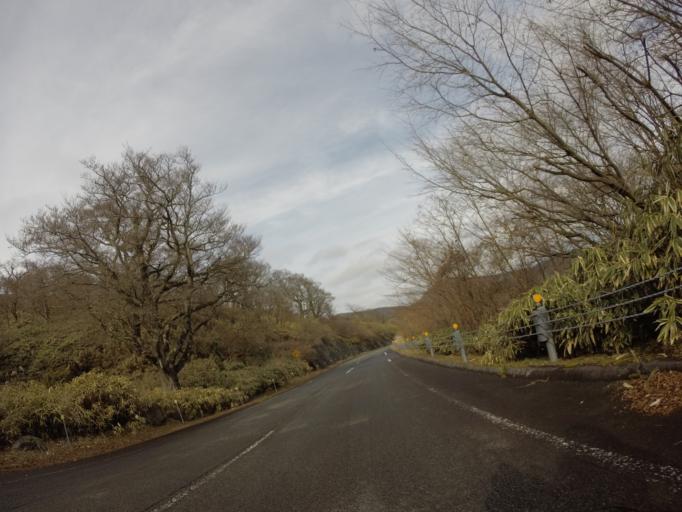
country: JP
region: Shizuoka
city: Heda
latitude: 34.8672
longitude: 138.8404
